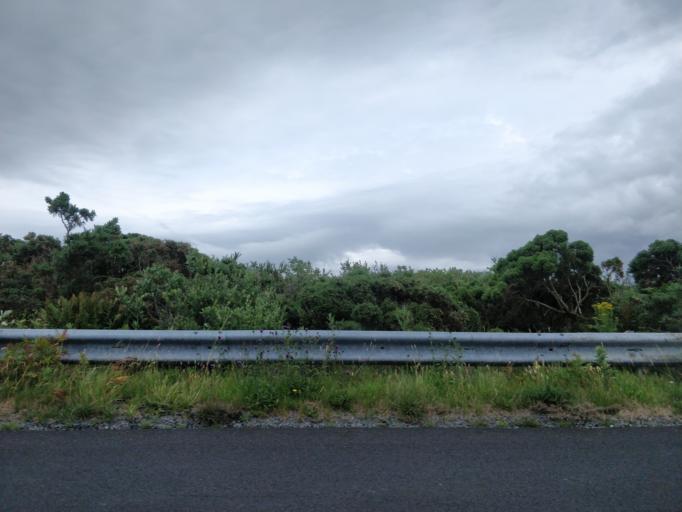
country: GB
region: Scotland
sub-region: Highland
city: Isle of Skye
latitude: 57.3685
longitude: -6.4412
